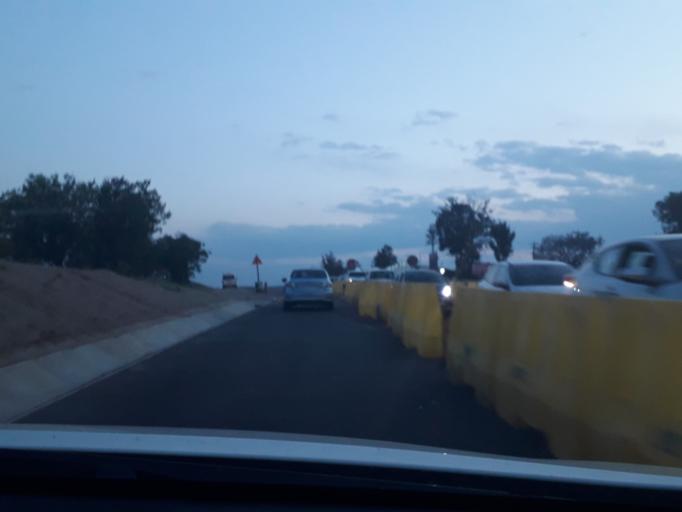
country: ZA
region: Gauteng
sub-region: City of Johannesburg Metropolitan Municipality
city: Midrand
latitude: -25.9842
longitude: 28.0765
